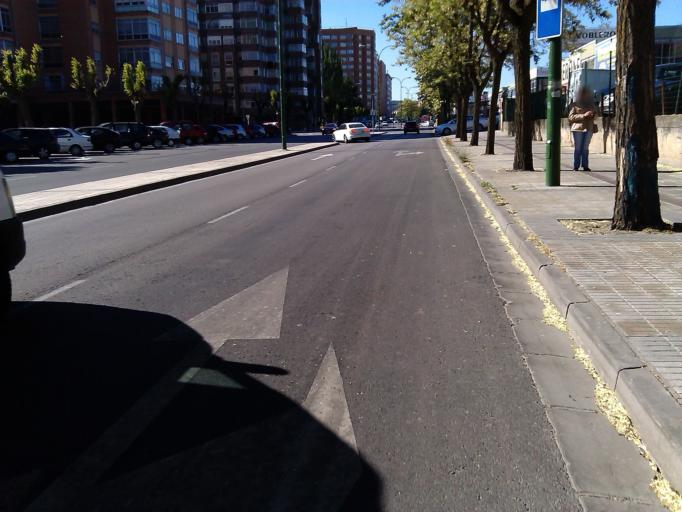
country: ES
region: Castille and Leon
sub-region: Provincia de Burgos
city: Burgos
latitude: 42.3512
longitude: -3.6609
